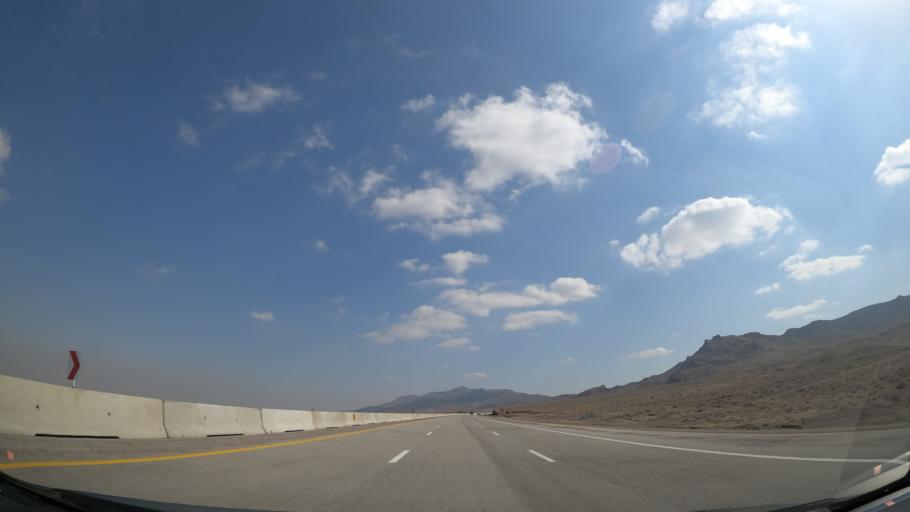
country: IR
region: Alborz
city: Eshtehard
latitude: 35.7069
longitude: 50.6070
